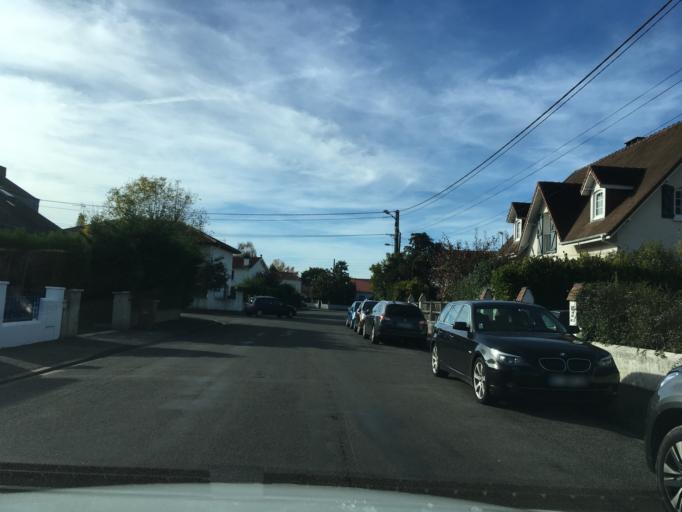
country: FR
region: Aquitaine
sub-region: Departement des Pyrenees-Atlantiques
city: Pau
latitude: 43.3237
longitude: -0.3650
